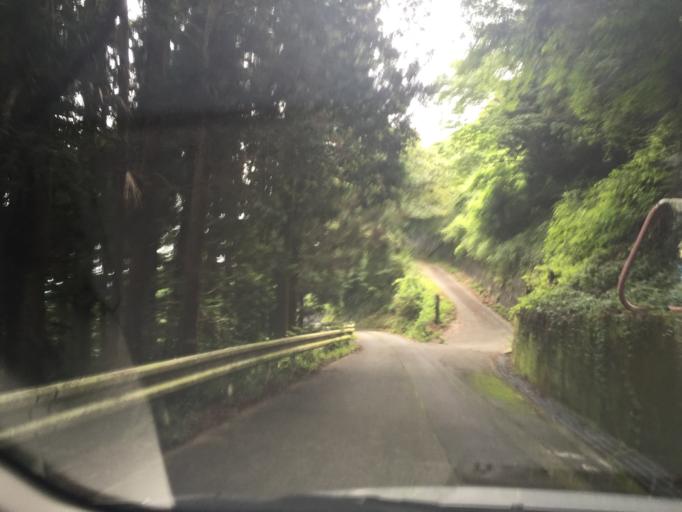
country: JP
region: Shizuoka
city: Kanaya
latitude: 34.8388
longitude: 138.0682
